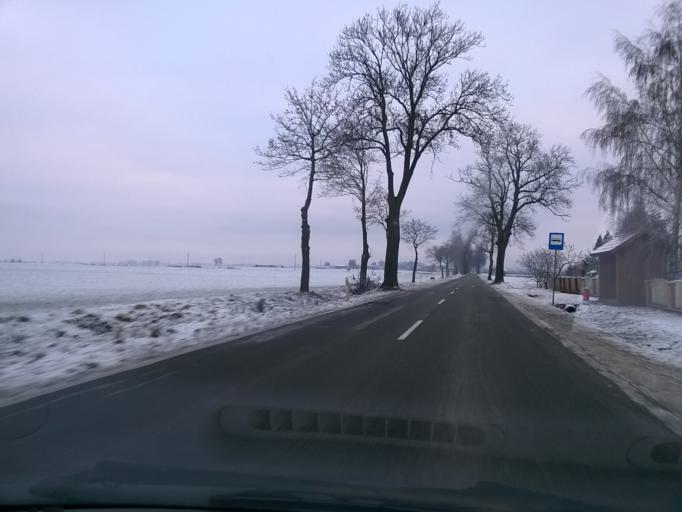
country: PL
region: Kujawsko-Pomorskie
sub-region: Powiat nakielski
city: Mrocza
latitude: 53.2129
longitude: 17.5922
